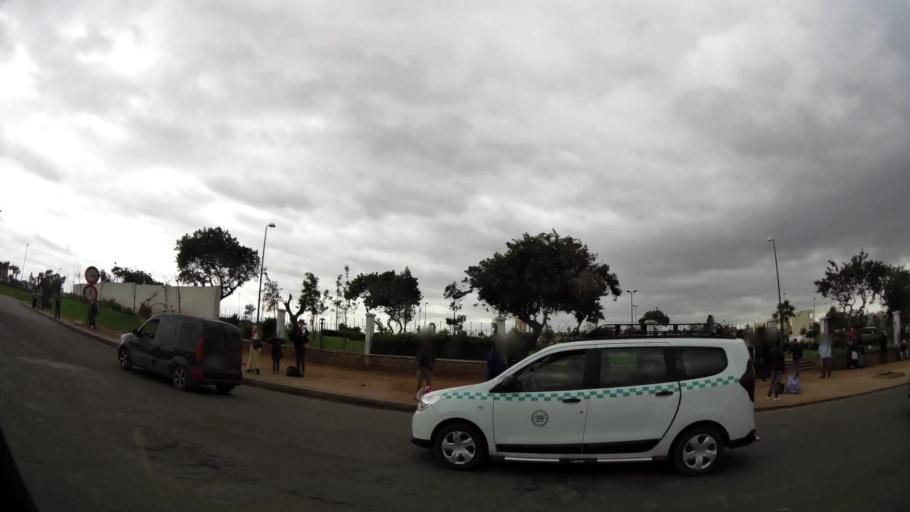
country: MA
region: Grand Casablanca
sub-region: Casablanca
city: Casablanca
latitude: 33.5699
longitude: -7.5772
